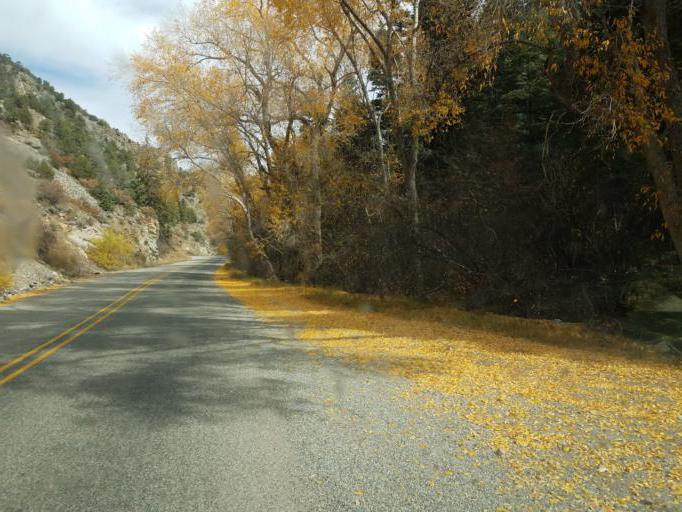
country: US
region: New Mexico
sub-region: Taos County
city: Arroyo Seco
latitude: 36.5419
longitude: -105.5566
